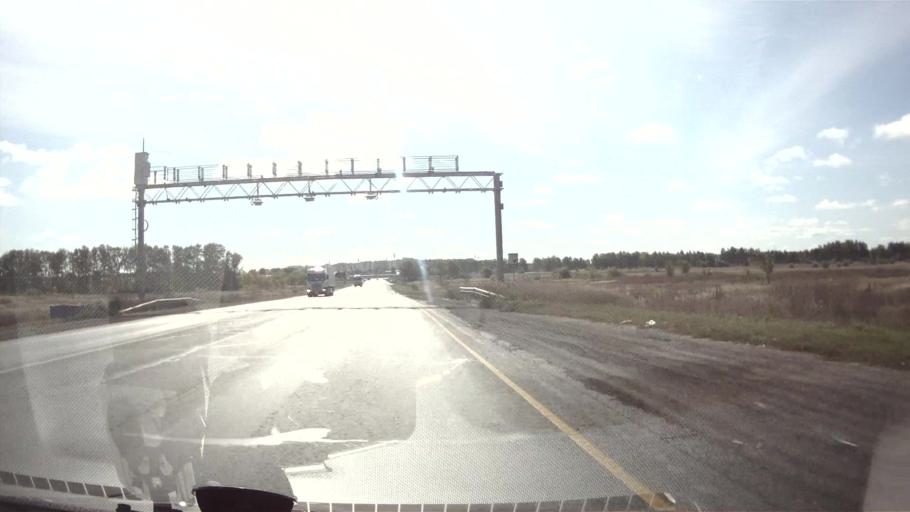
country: RU
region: Ulyanovsk
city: Isheyevka
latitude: 54.2980
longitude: 48.2473
